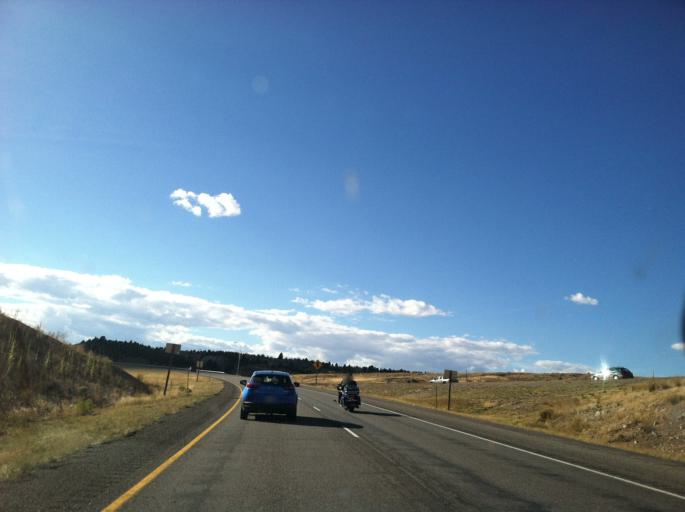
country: US
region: Montana
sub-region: Silver Bow County
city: Butte
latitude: 46.0047
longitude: -112.5721
